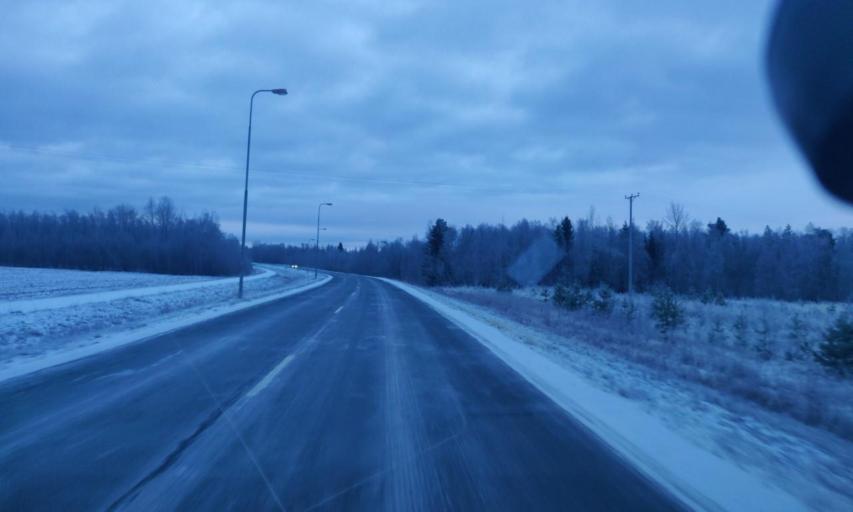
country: FI
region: Northern Ostrobothnia
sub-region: Oulu
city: Oulunsalo
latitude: 64.9744
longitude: 25.2920
